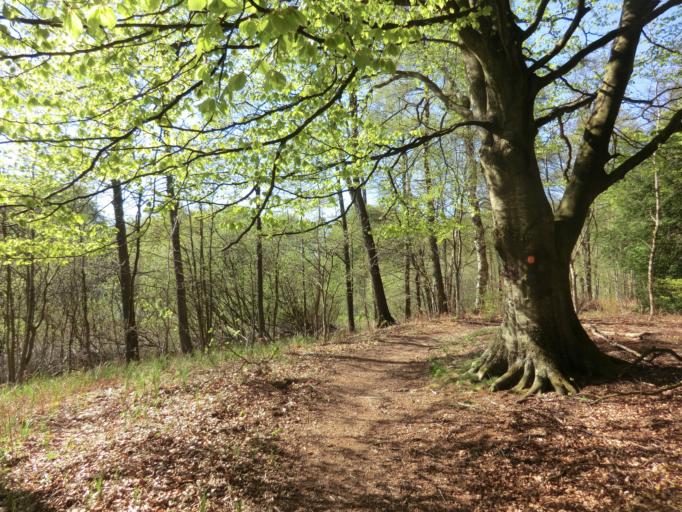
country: SE
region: Skane
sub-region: Sjobo Kommun
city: Sjoebo
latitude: 55.5736
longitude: 13.7193
